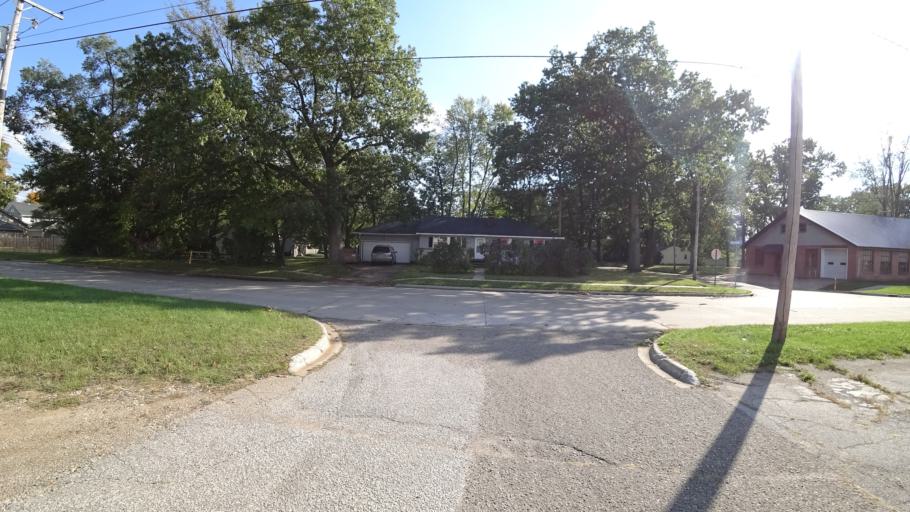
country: US
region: Michigan
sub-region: Saint Joseph County
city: Three Rivers
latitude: 41.9585
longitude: -85.6359
